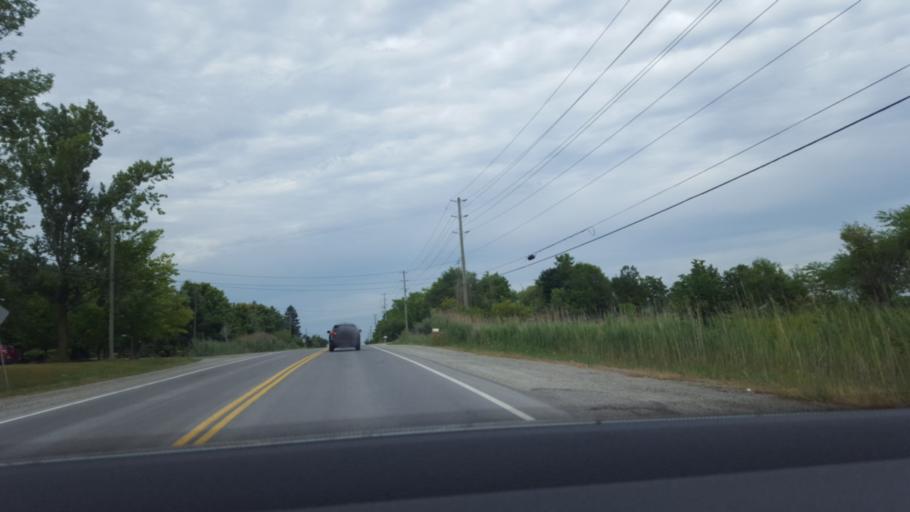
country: CA
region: Ontario
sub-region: Halton
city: Milton
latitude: 43.5169
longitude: -79.9481
